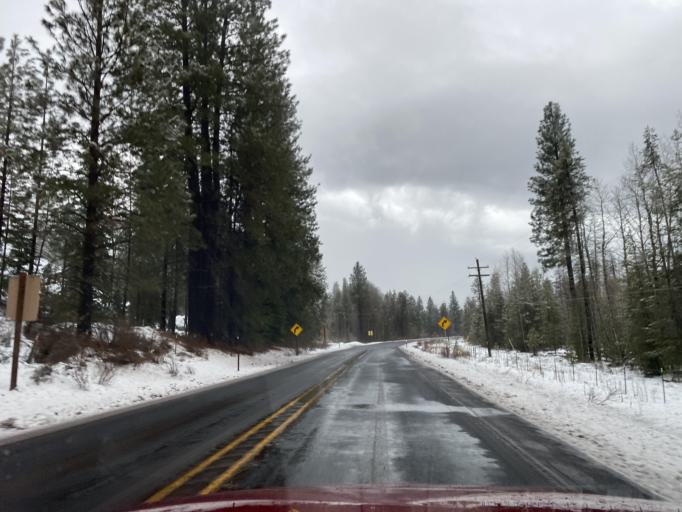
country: US
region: Oregon
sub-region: Klamath County
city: Klamath Falls
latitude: 42.4410
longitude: -122.1174
